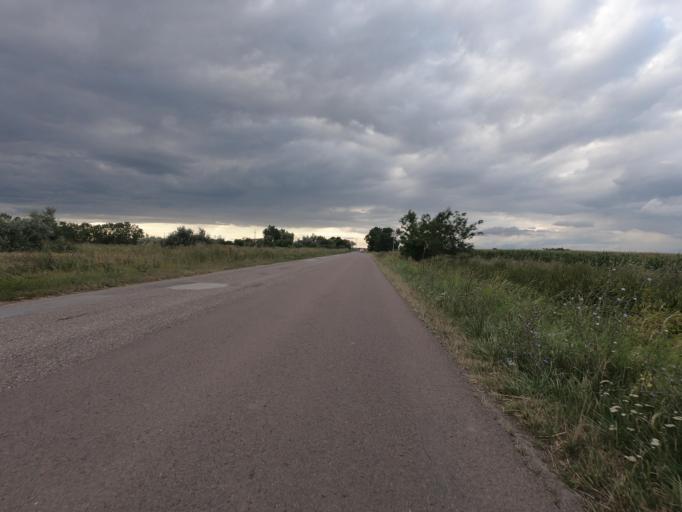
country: HU
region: Heves
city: Poroszlo
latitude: 47.6773
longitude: 20.6543
